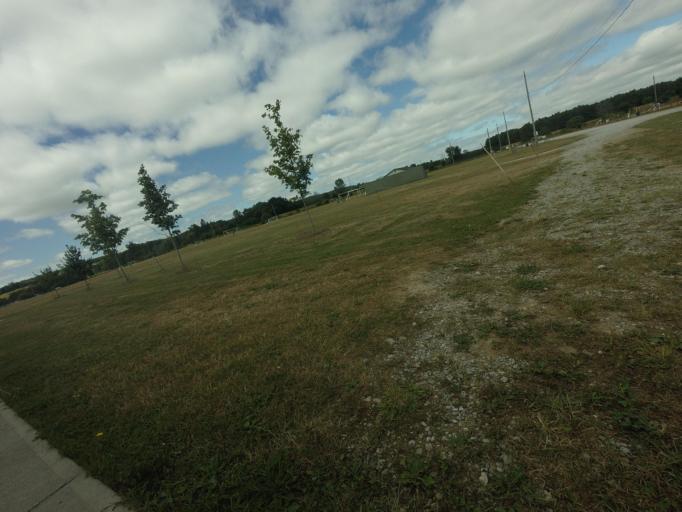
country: CA
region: Ontario
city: Uxbridge
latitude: 44.1264
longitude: -79.1234
